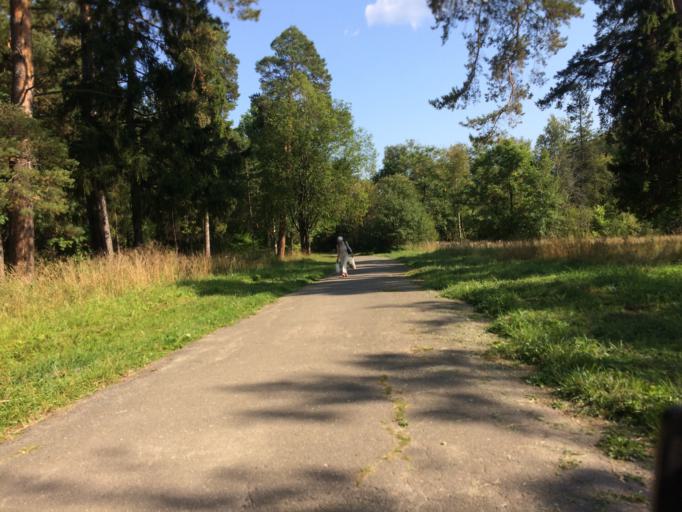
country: RU
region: Mariy-El
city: Yoshkar-Ola
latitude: 56.6169
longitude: 47.9381
